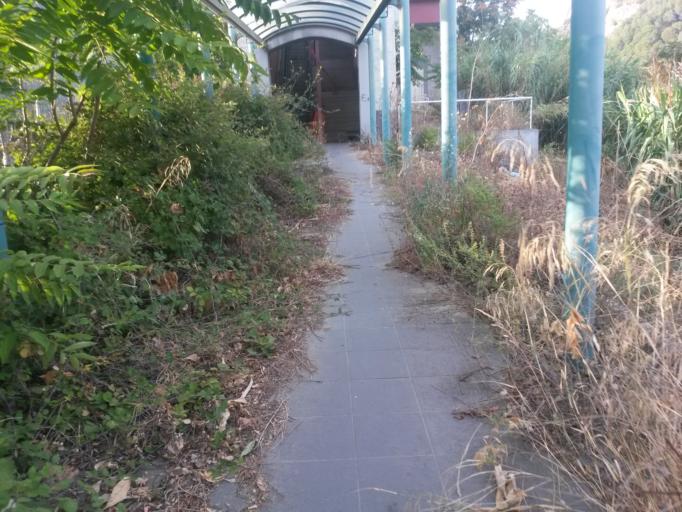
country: IT
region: Calabria
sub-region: Provincia di Catanzaro
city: Catanzaro
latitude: 38.8971
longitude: 16.6004
